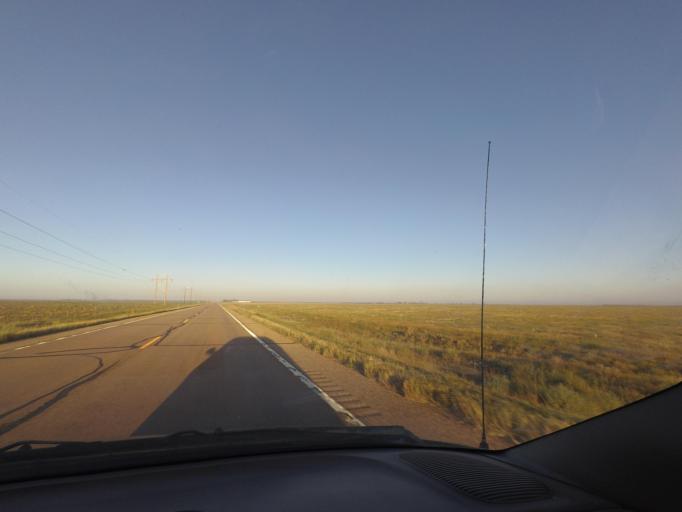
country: US
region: Colorado
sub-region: Yuma County
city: Yuma
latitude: 39.6558
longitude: -102.7305
